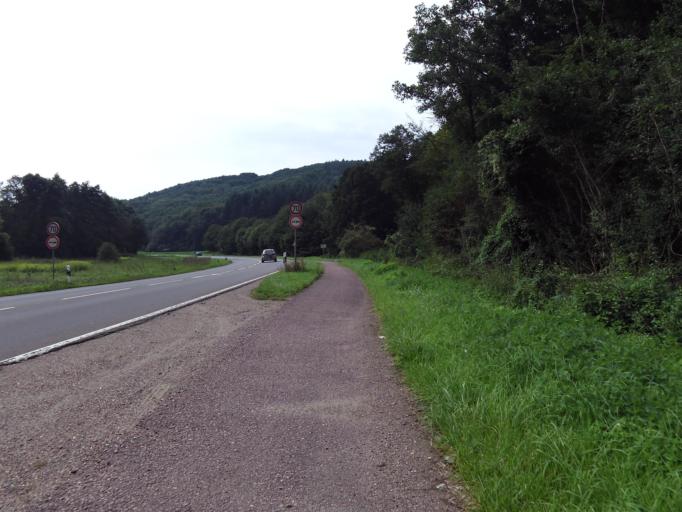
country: DE
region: Rheinland-Pfalz
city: Hochstatten
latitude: 49.7520
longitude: 7.8205
